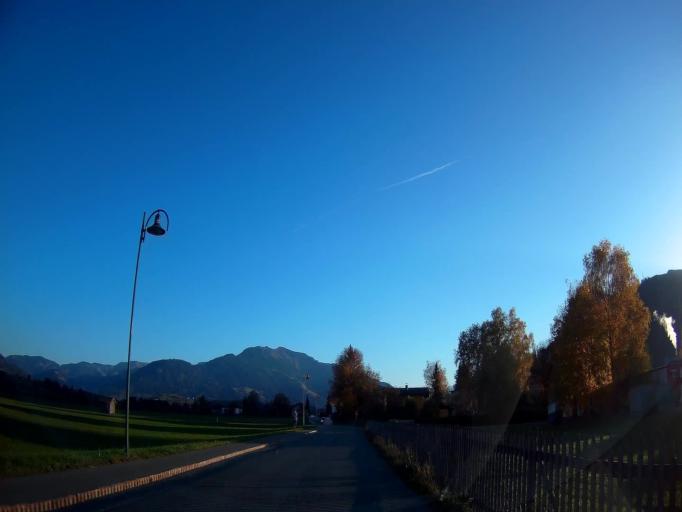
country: AT
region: Salzburg
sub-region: Politischer Bezirk Zell am See
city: Saalfelden am Steinernen Meer
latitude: 47.4433
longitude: 12.8179
